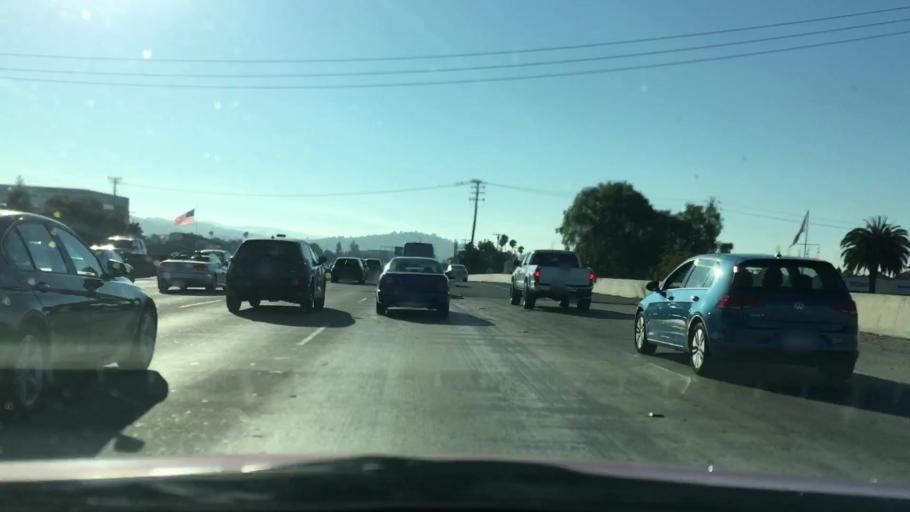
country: US
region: California
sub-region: San Mateo County
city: Redwood City
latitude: 37.4949
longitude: -122.2265
